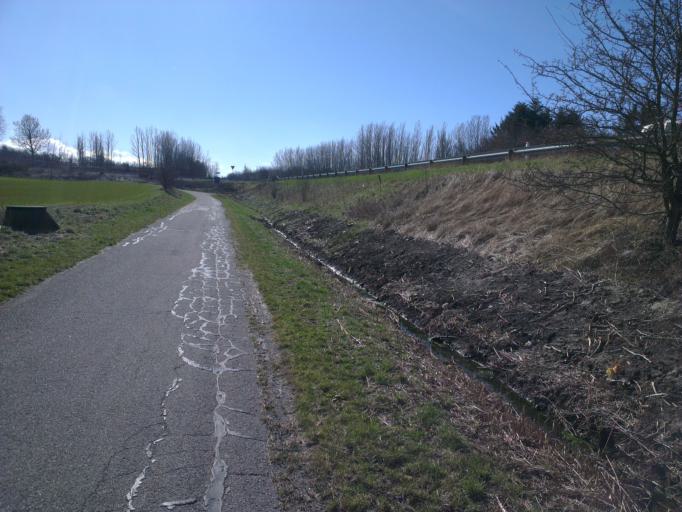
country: DK
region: Capital Region
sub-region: Frederikssund Kommune
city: Frederikssund
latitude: 55.8712
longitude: 12.0732
